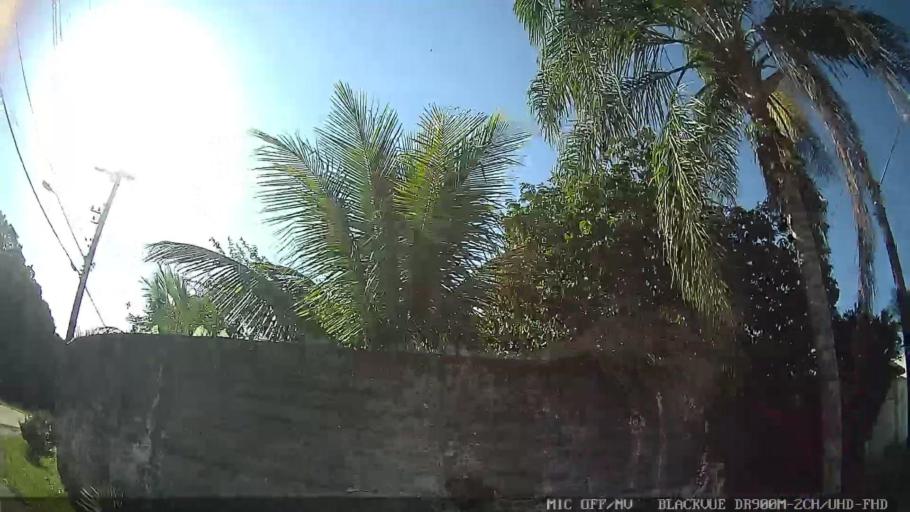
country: BR
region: Sao Paulo
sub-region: Guaruja
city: Guaruja
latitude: -23.9720
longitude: -46.2129
